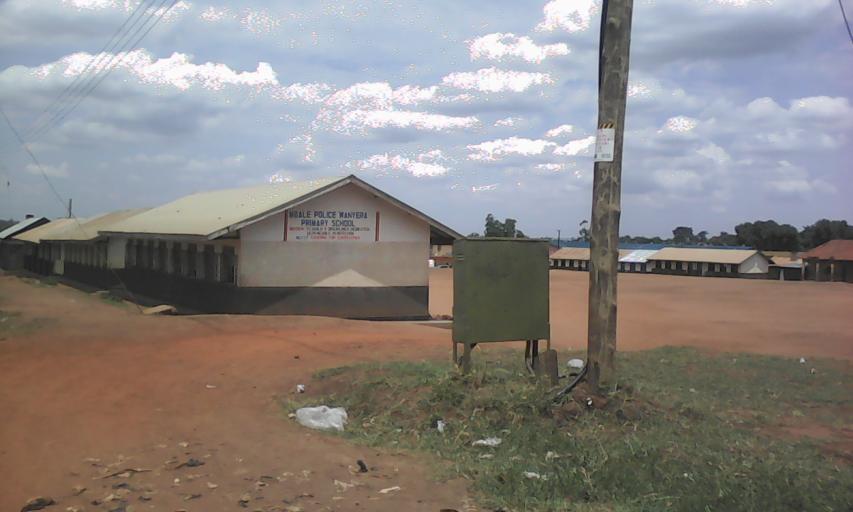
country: UG
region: Eastern Region
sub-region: Mbale District
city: Mbale
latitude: 1.0717
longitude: 34.1756
